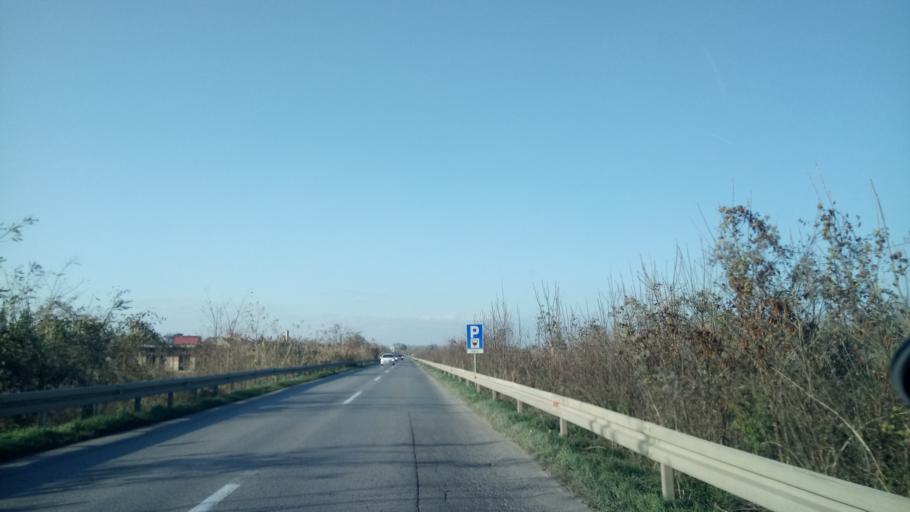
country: RS
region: Autonomna Pokrajina Vojvodina
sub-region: Juznobacki Okrug
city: Sremski Karlovci
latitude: 45.2002
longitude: 19.9424
